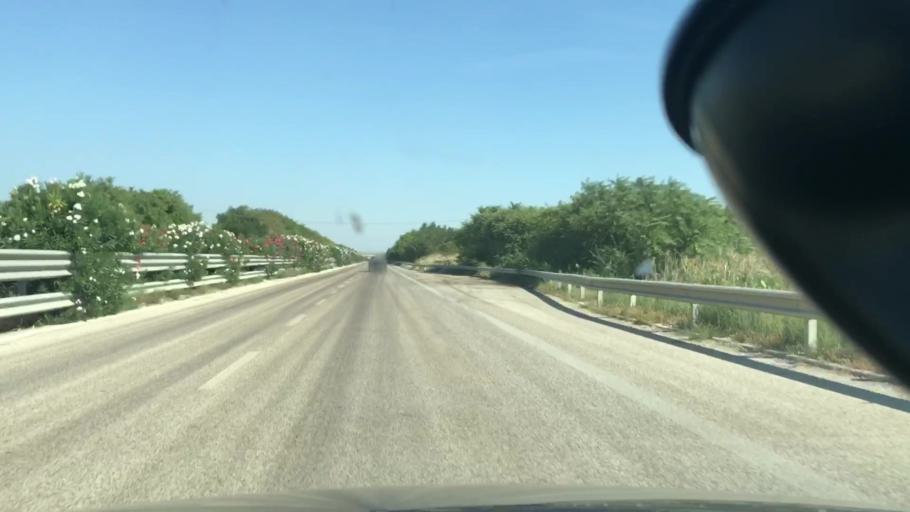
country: IT
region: Apulia
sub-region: Provincia di Foggia
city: Ascoli Satriano
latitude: 41.2816
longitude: 15.5540
